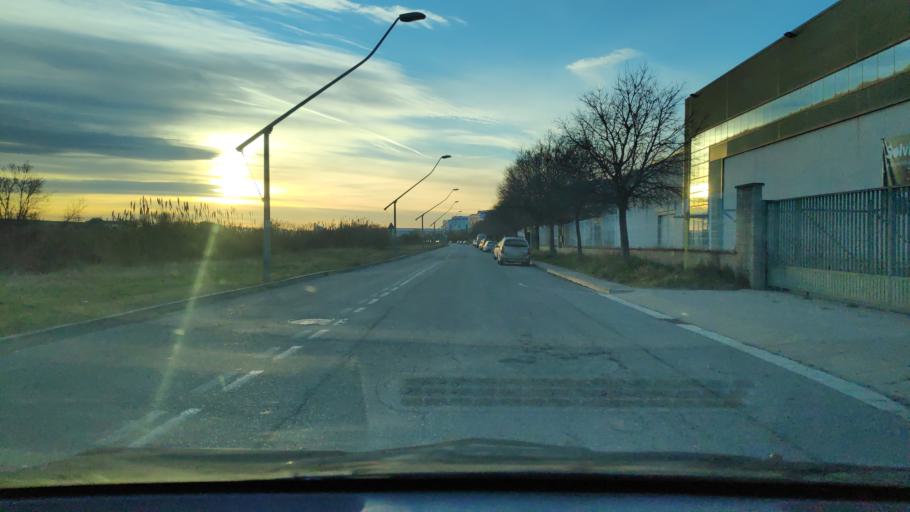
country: ES
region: Catalonia
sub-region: Provincia de Barcelona
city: Montmelo
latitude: 41.5465
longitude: 2.2436
